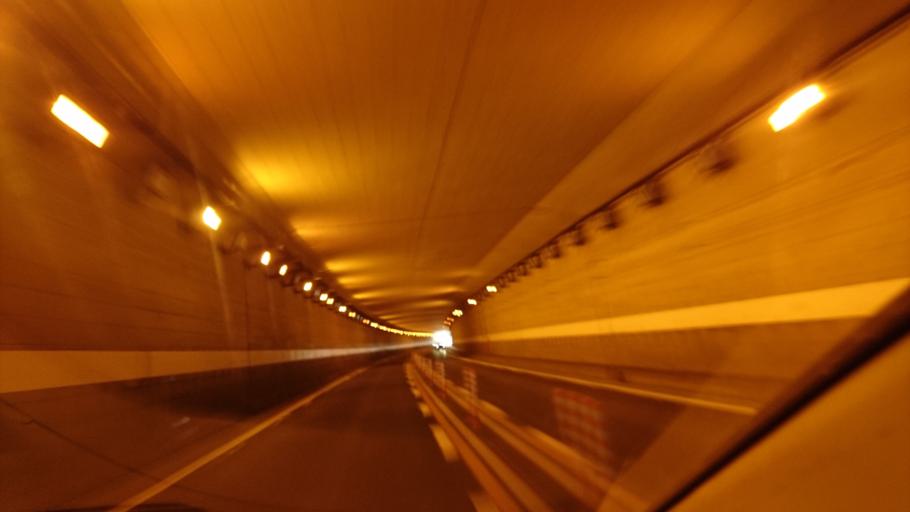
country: JP
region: Iwate
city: Kitakami
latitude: 39.2937
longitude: 140.9713
